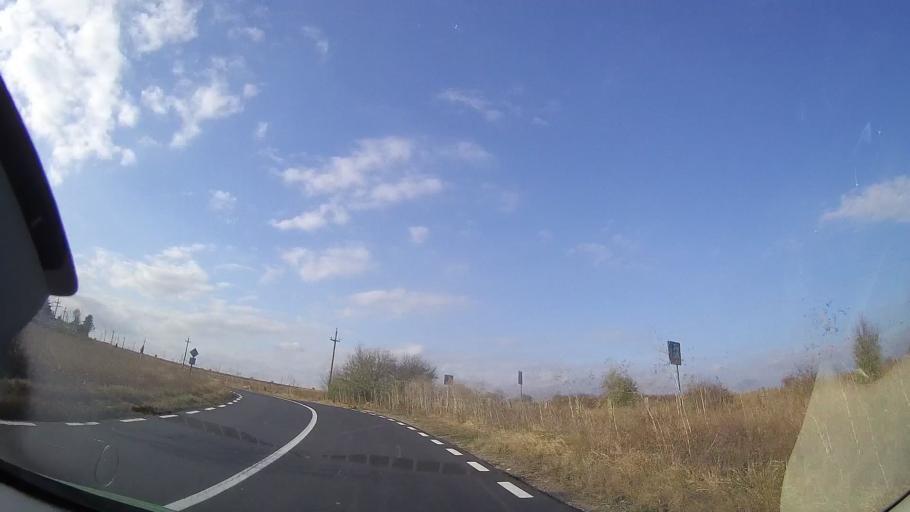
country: RO
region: Constanta
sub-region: Comuna Limanu
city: Limanu
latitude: 43.8233
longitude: 28.5231
